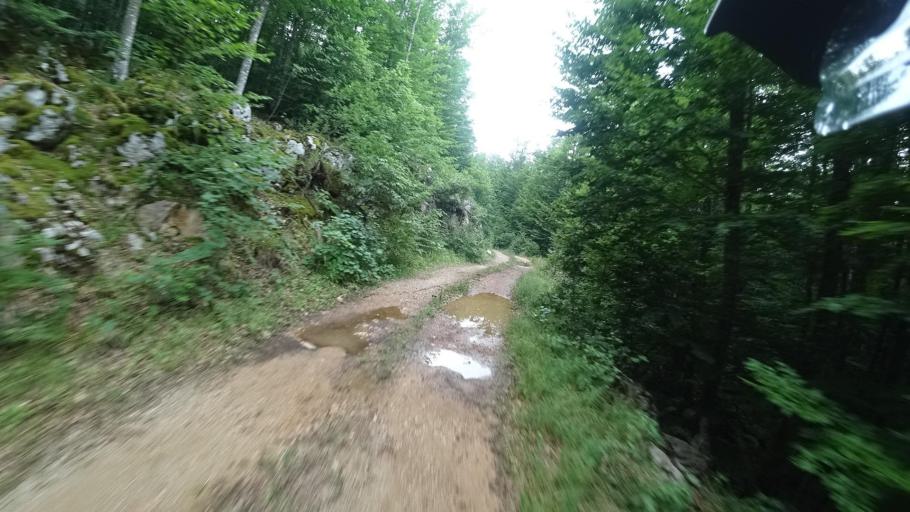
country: BA
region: Federation of Bosnia and Herzegovina
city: Bihac
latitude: 44.6449
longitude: 15.7626
